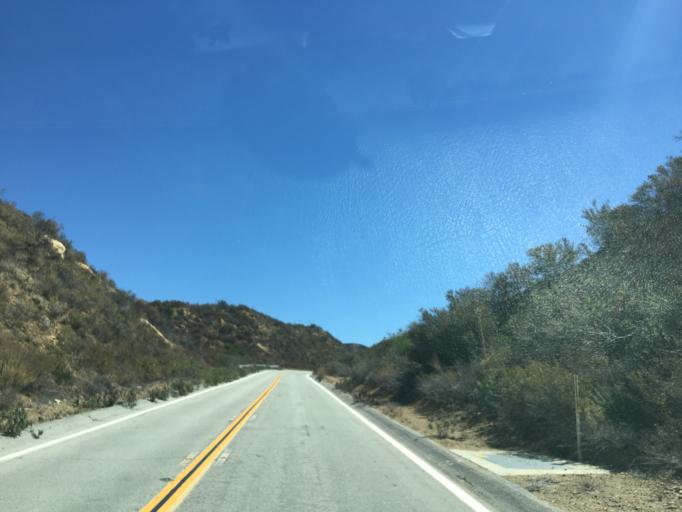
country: US
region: California
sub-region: Los Angeles County
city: Castaic
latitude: 34.5592
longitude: -118.5575
